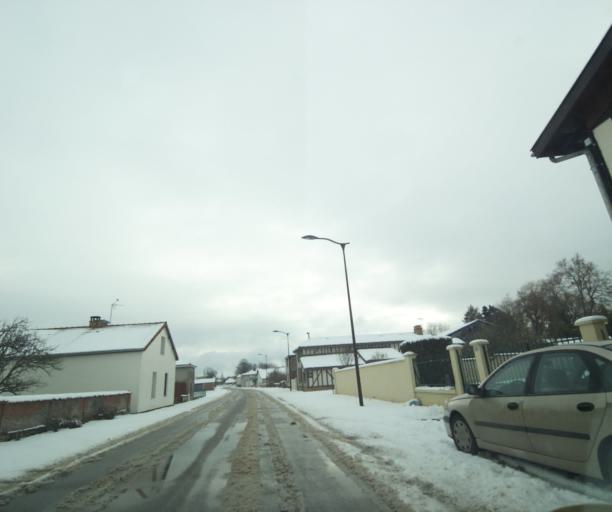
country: FR
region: Champagne-Ardenne
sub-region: Departement de la Haute-Marne
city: Montier-en-Der
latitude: 48.4358
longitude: 4.7156
